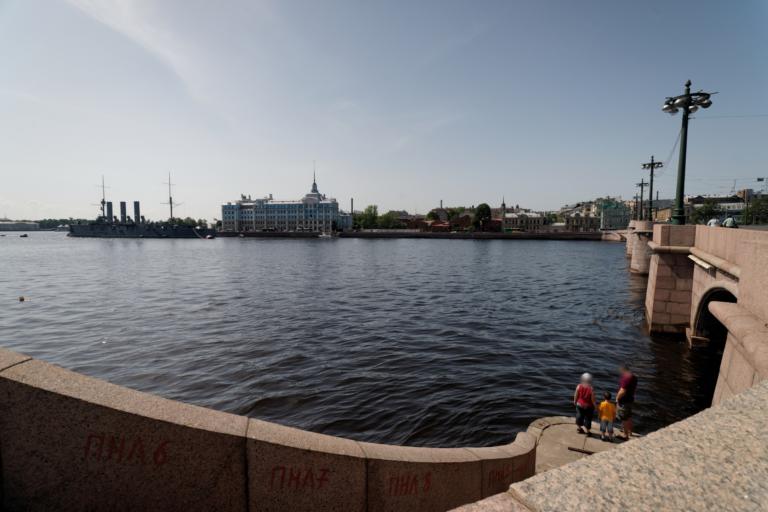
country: RU
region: Leningrad
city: Finlyandskiy
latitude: 59.9578
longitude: 30.3392
